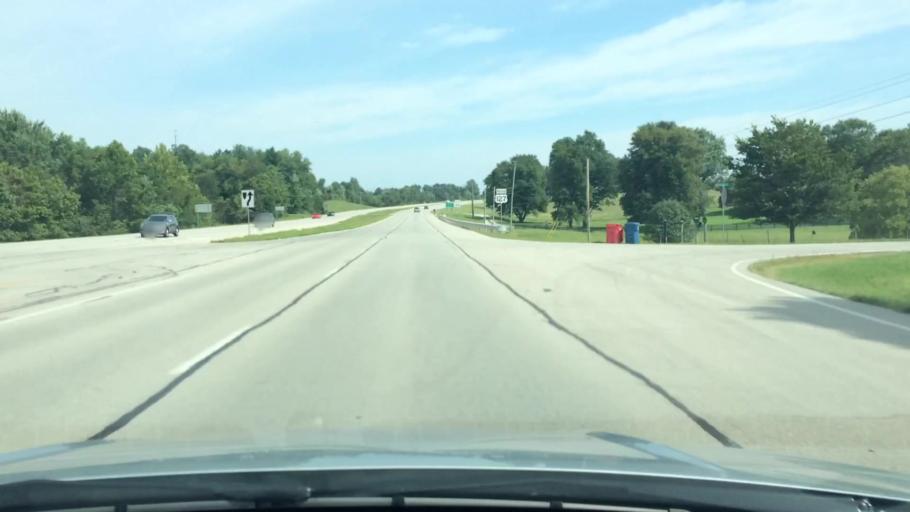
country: US
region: Kentucky
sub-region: Anderson County
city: Lawrenceburg
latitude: 38.0982
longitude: -84.9191
